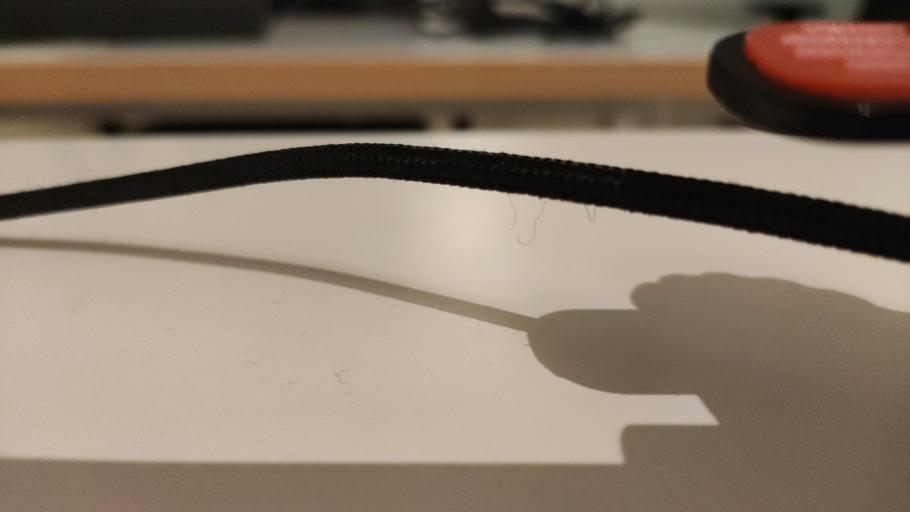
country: RU
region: Moskovskaya
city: Orekhovo-Zuyevo
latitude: 55.8037
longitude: 38.9726
